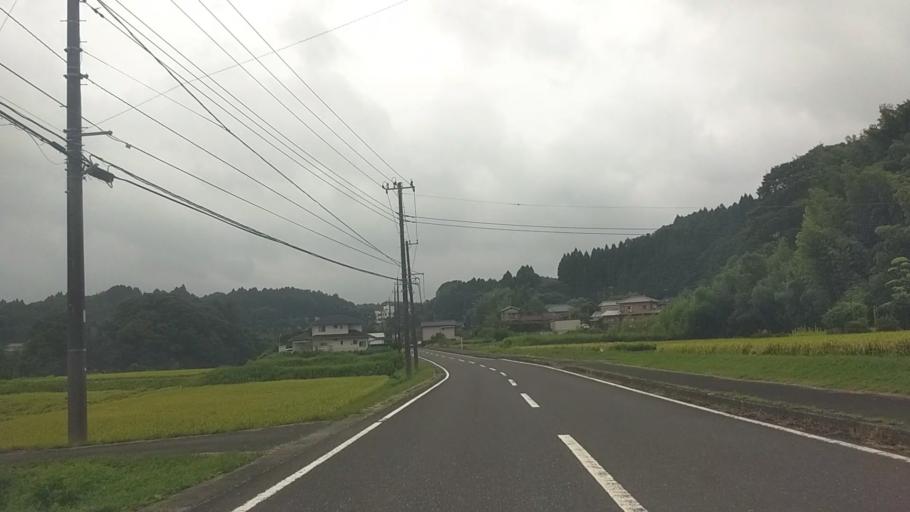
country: JP
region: Chiba
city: Kawaguchi
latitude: 35.2574
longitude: 140.0566
